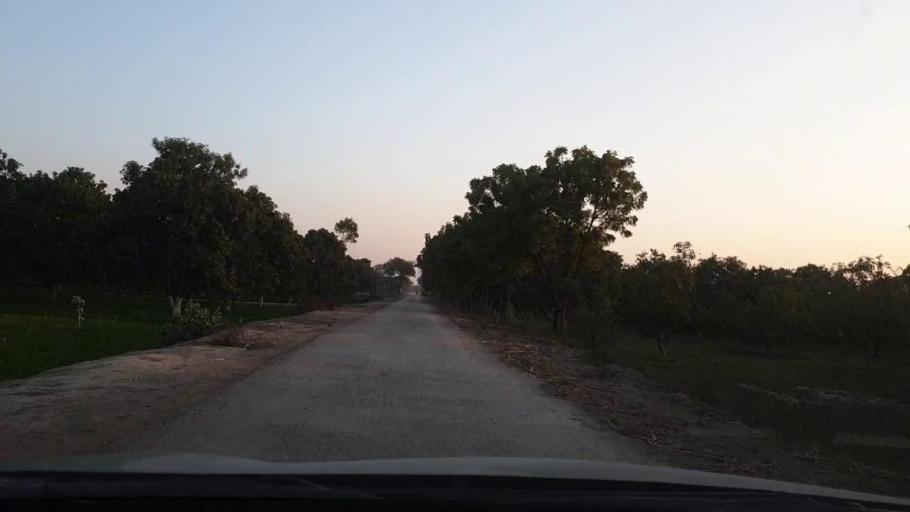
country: PK
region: Sindh
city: Tando Allahyar
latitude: 25.5230
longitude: 68.7462
